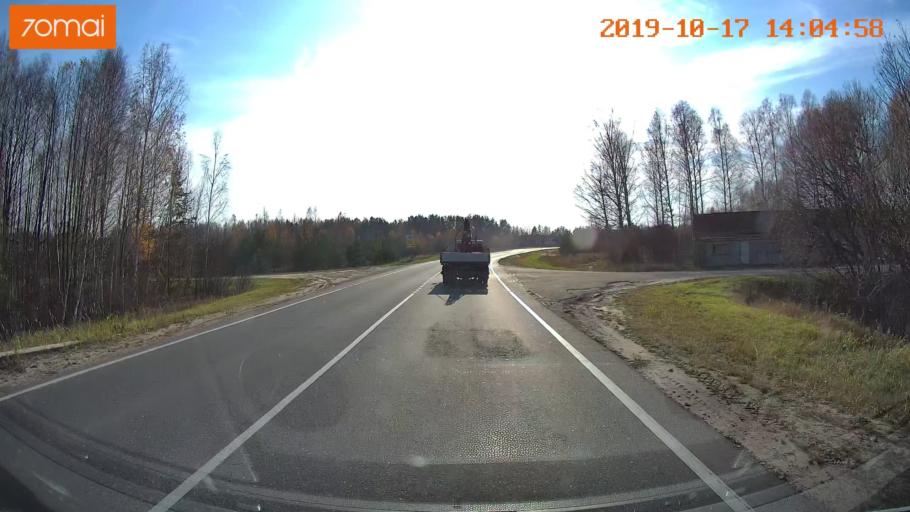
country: RU
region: Rjazan
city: Spas-Klepiki
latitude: 55.1202
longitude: 40.1329
